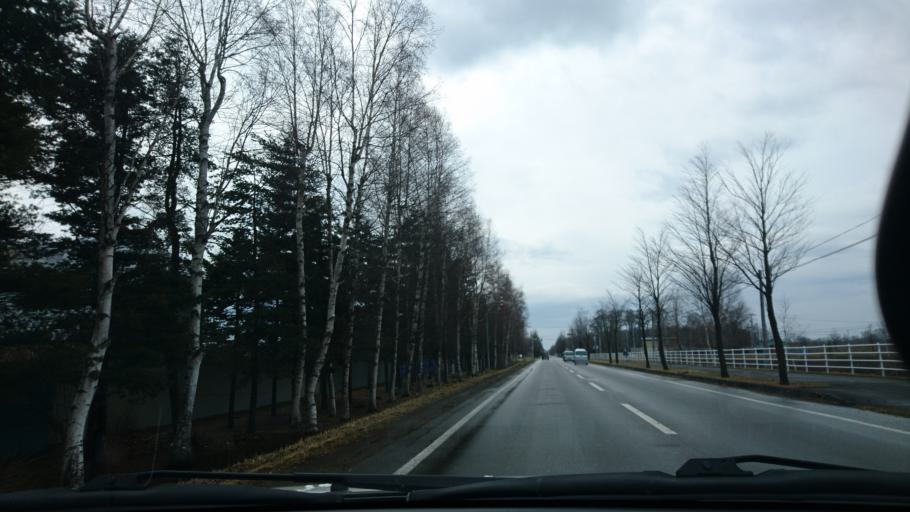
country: JP
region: Hokkaido
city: Otofuke
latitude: 42.9928
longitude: 143.1891
